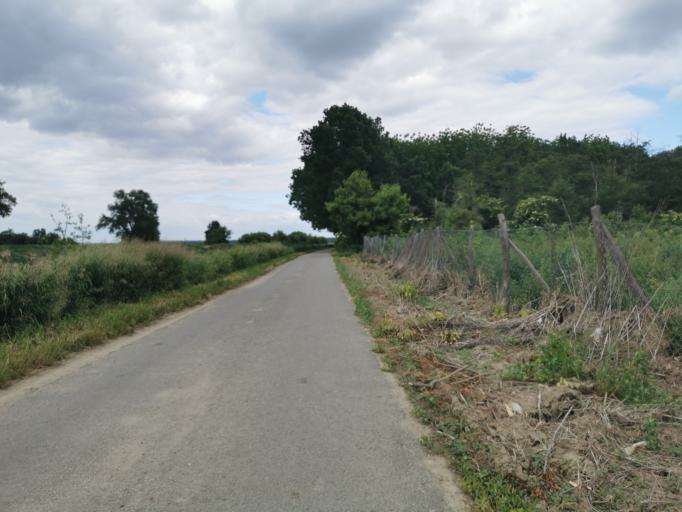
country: CZ
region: South Moravian
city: Straznice
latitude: 48.9329
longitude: 17.2991
